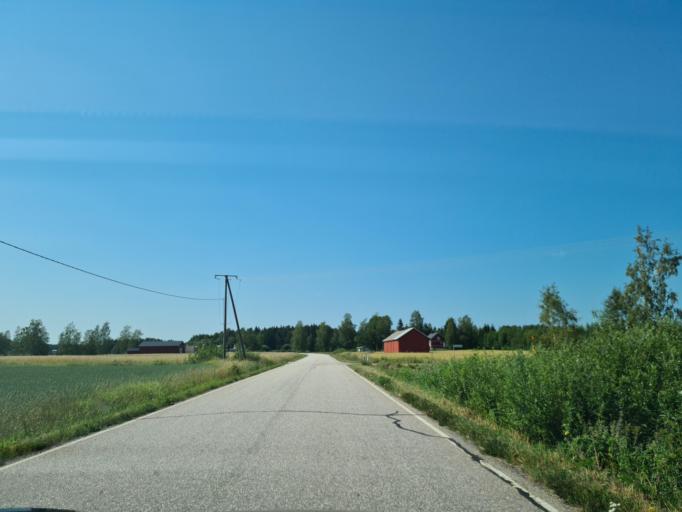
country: FI
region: Varsinais-Suomi
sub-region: Loimaa
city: Aura
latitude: 60.6061
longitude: 22.6288
